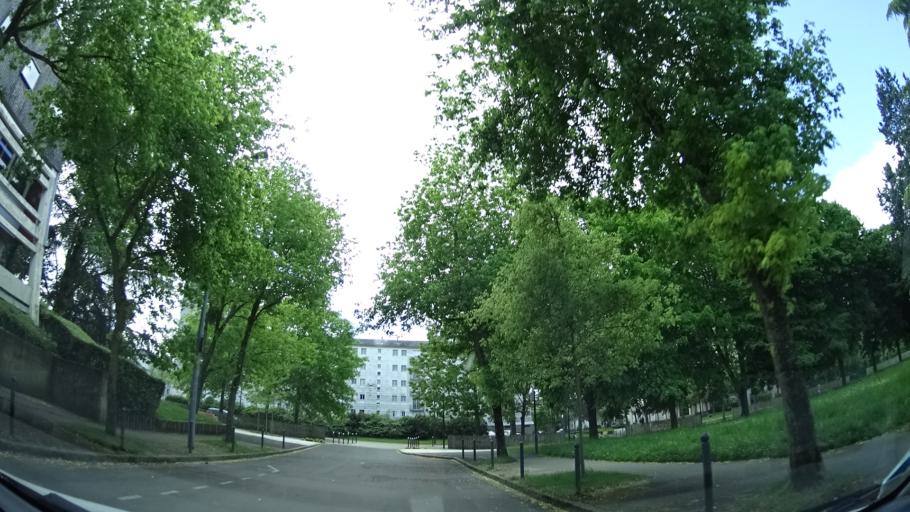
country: FR
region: Brittany
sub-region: Departement d'Ille-et-Vilaine
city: Rennes
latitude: 48.1285
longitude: -1.6588
